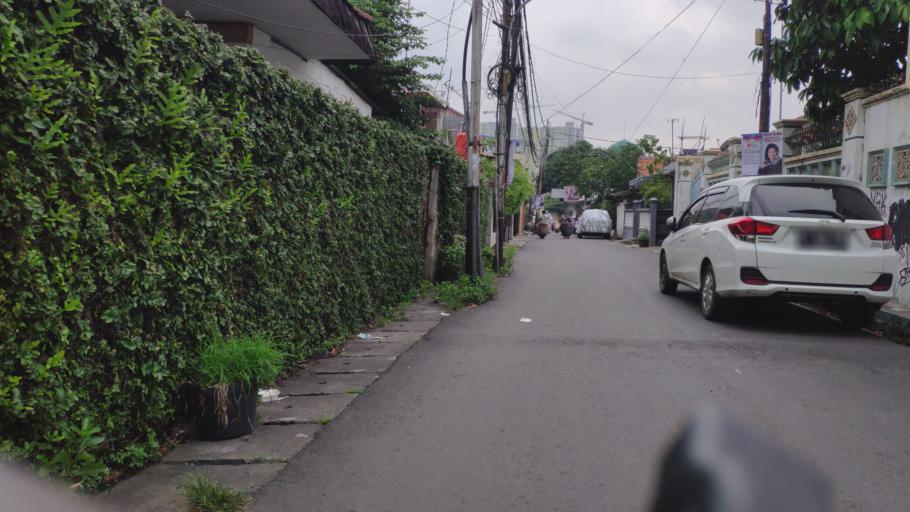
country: ID
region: Jakarta Raya
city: Jakarta
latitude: -6.2139
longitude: 106.8407
